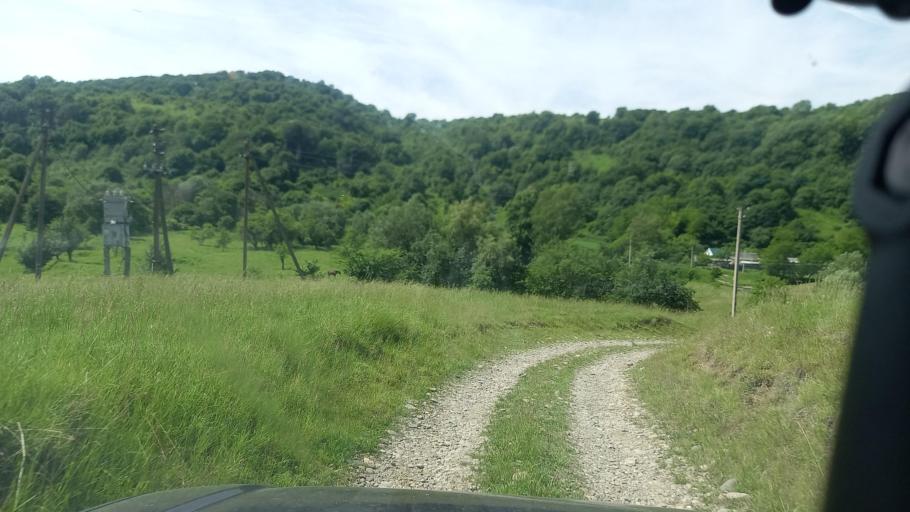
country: RU
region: Karachayevo-Cherkesiya
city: Kurdzhinovo
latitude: 44.1425
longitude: 41.0568
